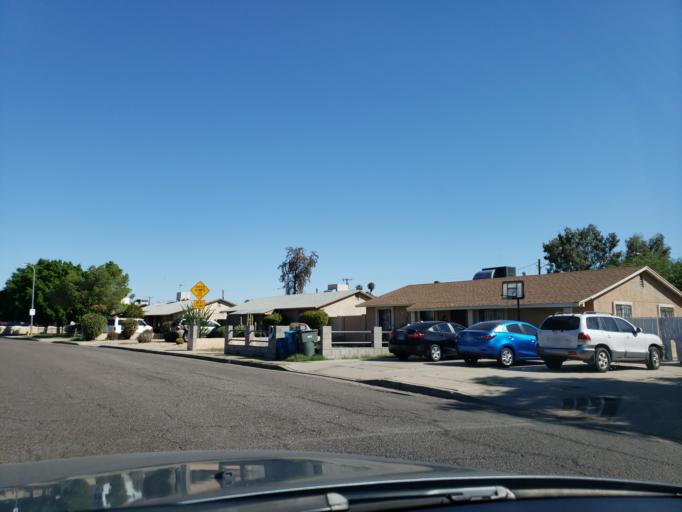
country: US
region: Arizona
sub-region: Maricopa County
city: Glendale
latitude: 33.4816
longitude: -112.1596
